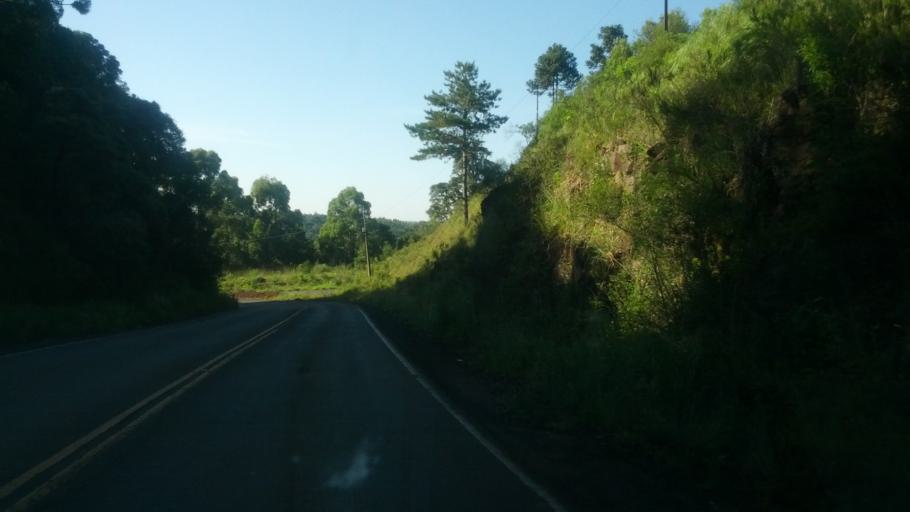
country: BR
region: Santa Catarina
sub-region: Lages
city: Lages
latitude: -27.9560
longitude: -50.4898
